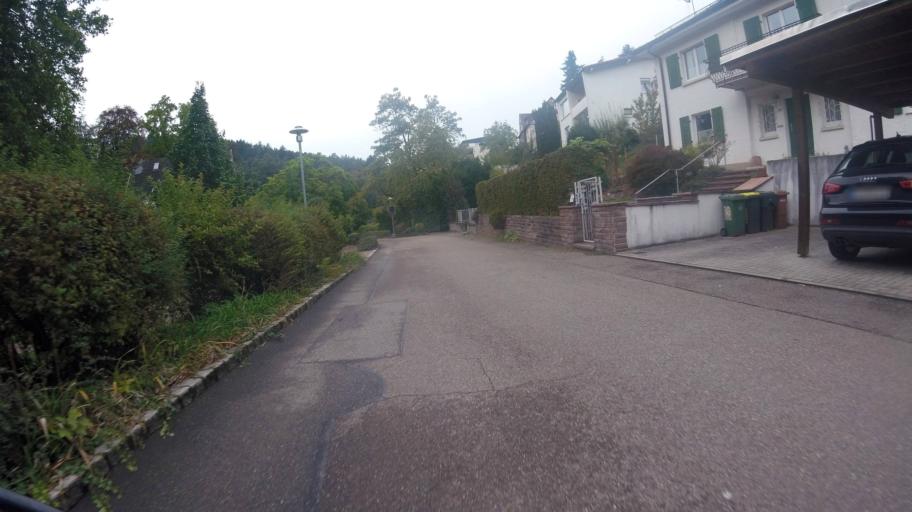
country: DE
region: Baden-Wuerttemberg
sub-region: Karlsruhe Region
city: Gernsbach
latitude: 48.7614
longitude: 8.3436
